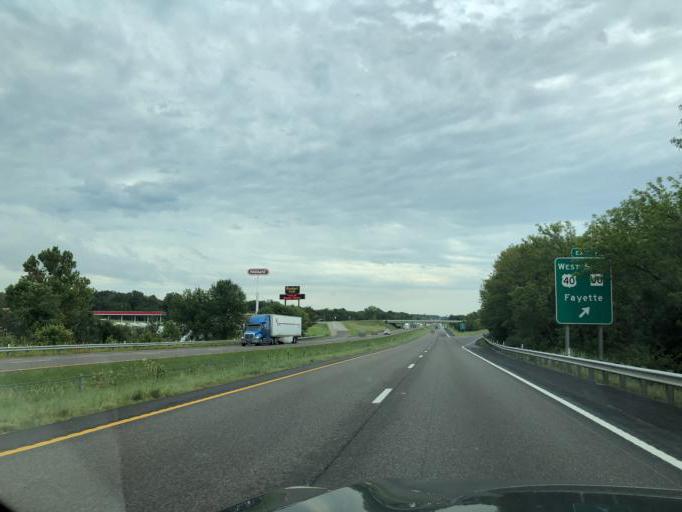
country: US
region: Missouri
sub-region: Boone County
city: Columbia
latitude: 38.9718
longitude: -92.4360
